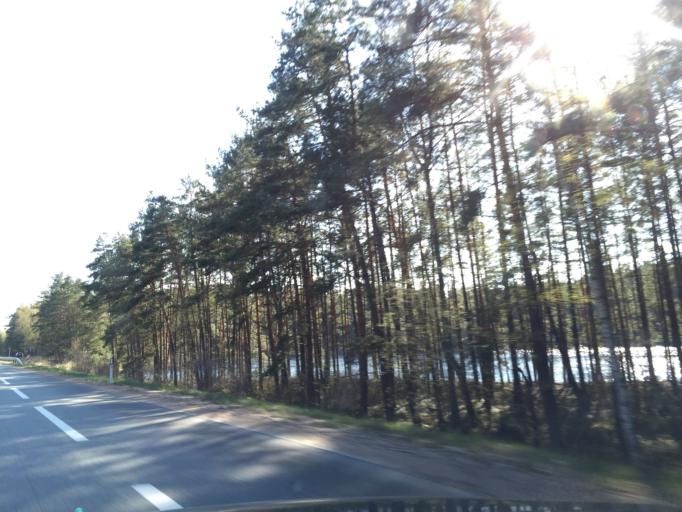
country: LV
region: Adazi
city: Adazi
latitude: 57.1302
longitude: 24.3312
